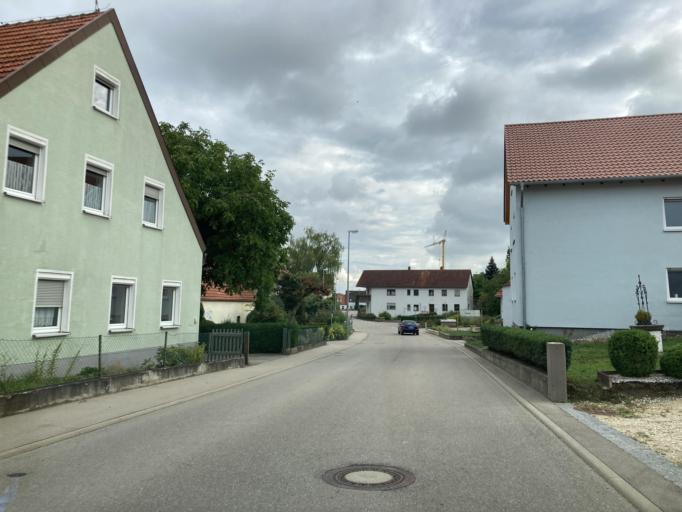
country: DE
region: Bavaria
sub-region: Swabia
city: Forheim
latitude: 48.7858
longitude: 10.4146
